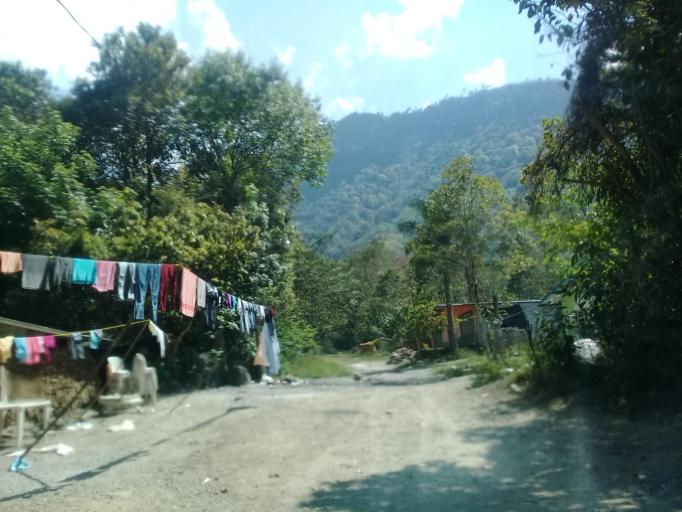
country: MX
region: Veracruz
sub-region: Tlilapan
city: Tonalixco
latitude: 18.8022
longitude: -97.0697
